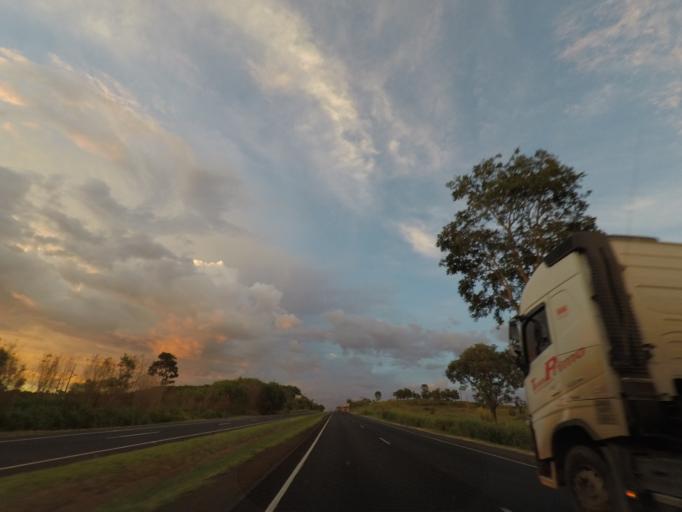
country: BR
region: Minas Gerais
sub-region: Uberaba
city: Uberaba
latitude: -19.5976
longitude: -48.0262
